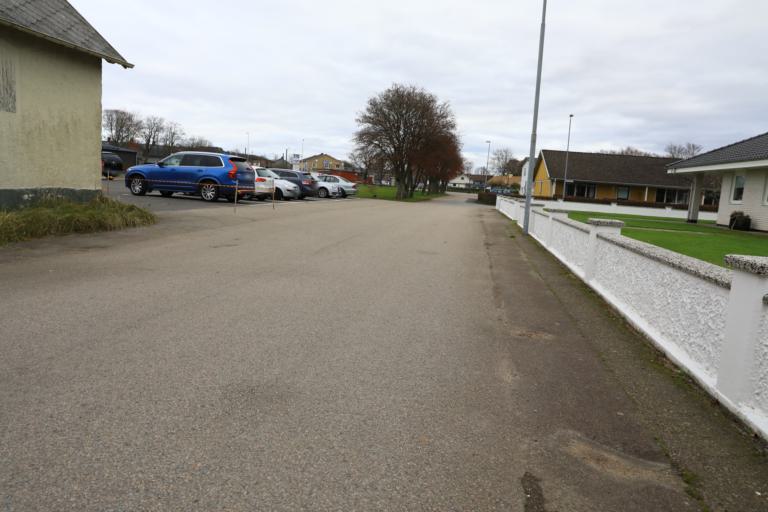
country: SE
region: Halland
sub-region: Varbergs Kommun
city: Tvaaker
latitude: 57.0418
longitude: 12.3966
